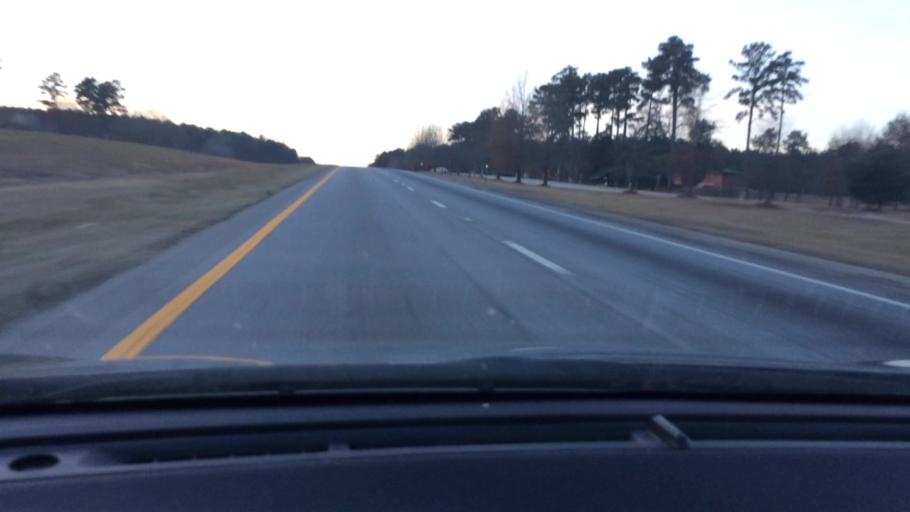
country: US
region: South Carolina
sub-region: Laurens County
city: Joanna
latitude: 34.4114
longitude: -81.7039
